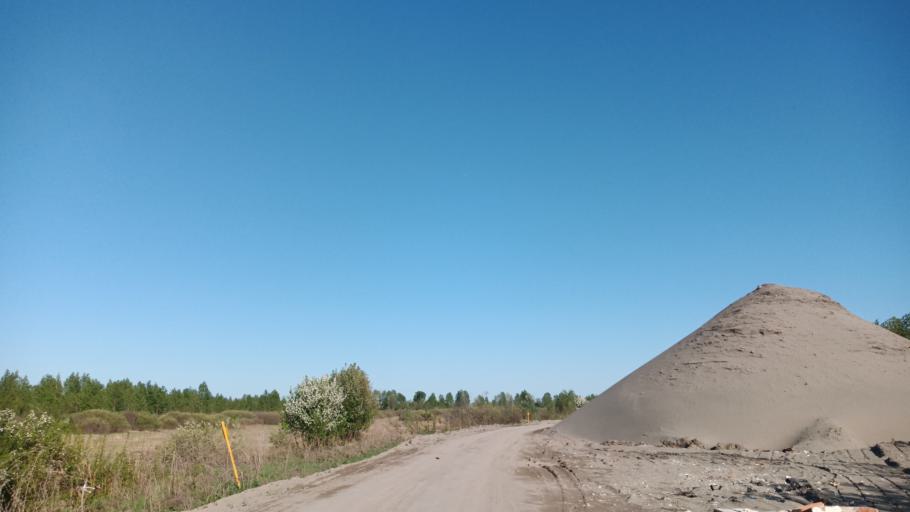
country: RU
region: Altai Krai
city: Zaton
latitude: 53.3111
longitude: 83.8198
